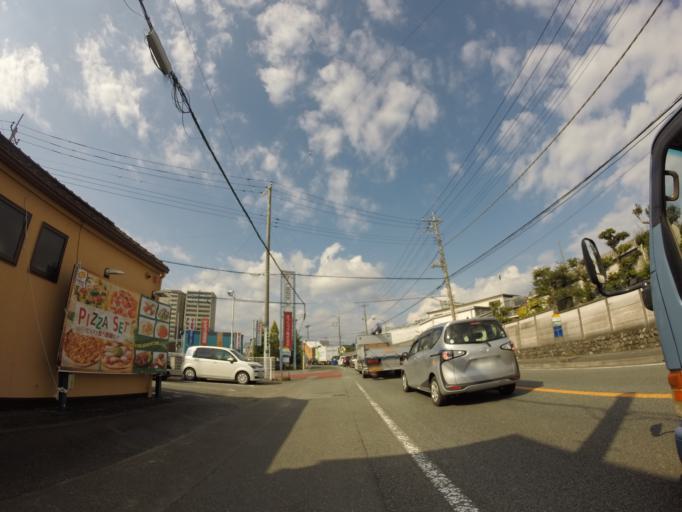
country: JP
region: Shizuoka
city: Fujinomiya
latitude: 35.2206
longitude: 138.6200
